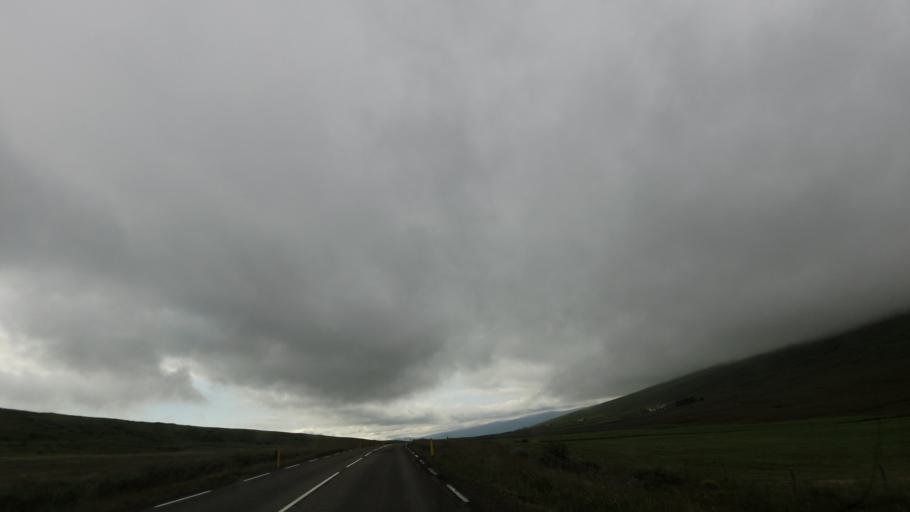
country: IS
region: Northeast
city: Laugar
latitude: 65.7768
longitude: -17.5800
